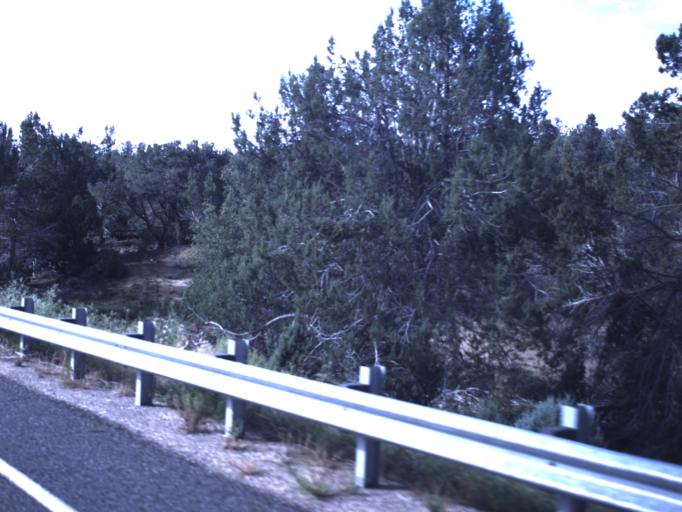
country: US
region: Utah
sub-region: Kane County
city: Kanab
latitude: 37.2560
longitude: -112.7648
